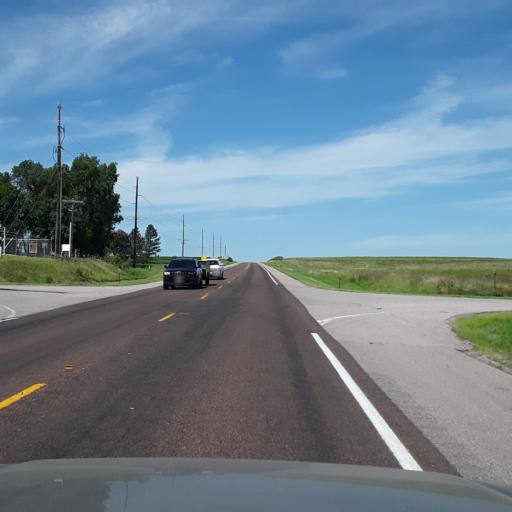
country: US
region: Nebraska
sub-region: Seward County
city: Milford
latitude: 40.8866
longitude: -96.8719
